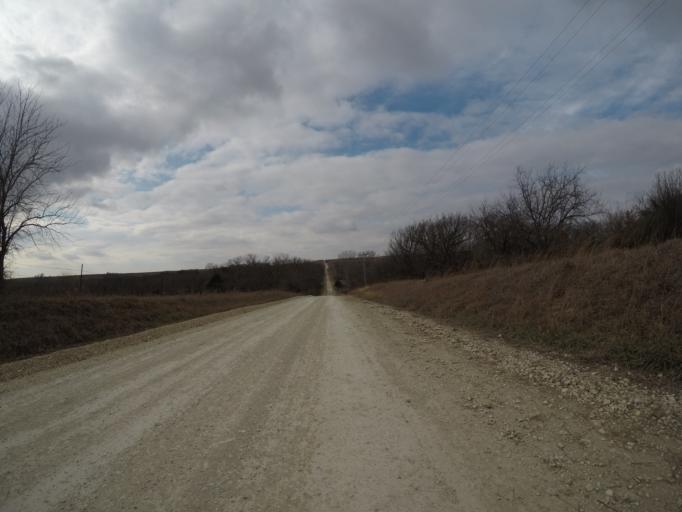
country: US
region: Kansas
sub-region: Morris County
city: Council Grove
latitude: 38.7681
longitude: -96.3051
